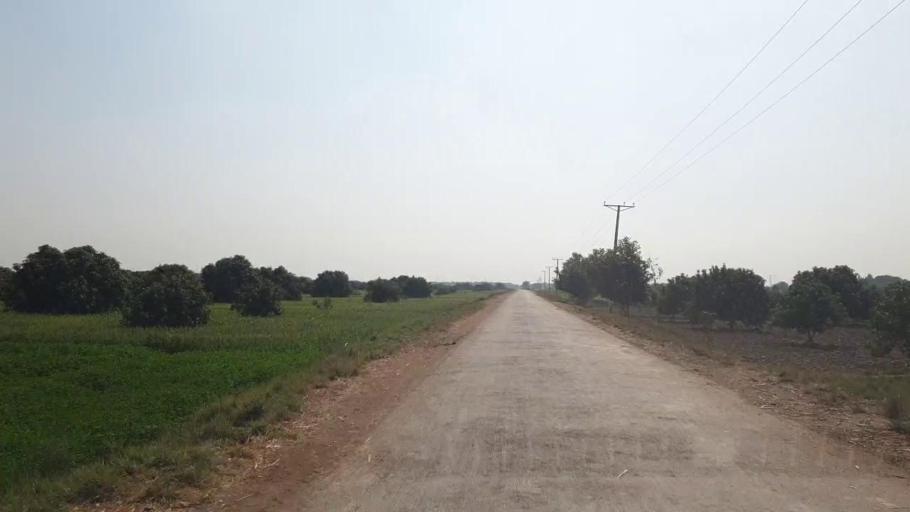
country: PK
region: Sindh
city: Chambar
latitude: 25.4003
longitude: 68.8958
